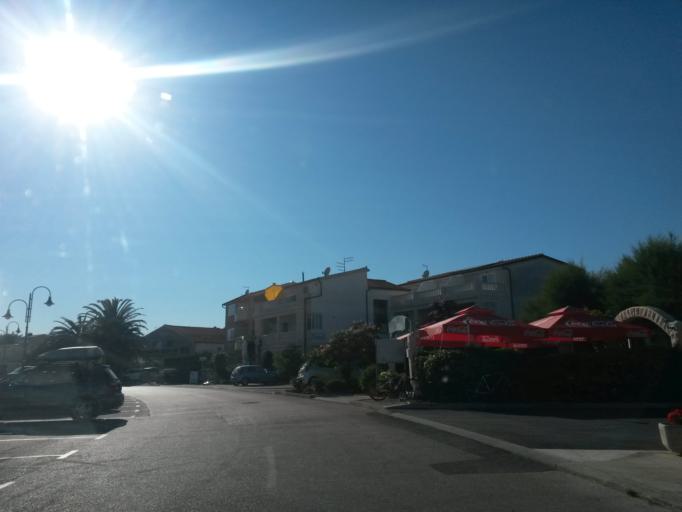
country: HR
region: Sibensko-Kniniska
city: Rogoznica
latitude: 43.5341
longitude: 15.9637
